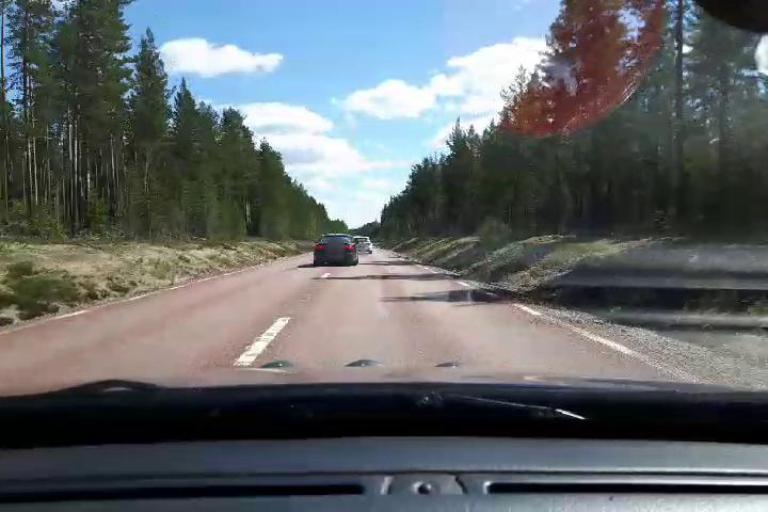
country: SE
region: Gaevleborg
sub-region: Ljusdals Kommun
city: Farila
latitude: 61.8141
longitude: 15.7654
